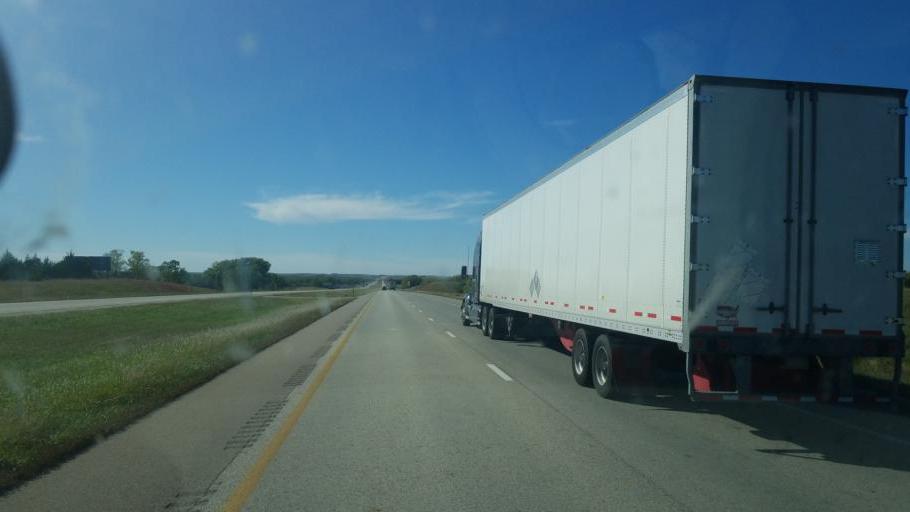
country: US
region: Kansas
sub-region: Saline County
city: Salina
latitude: 38.8780
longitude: -97.7688
